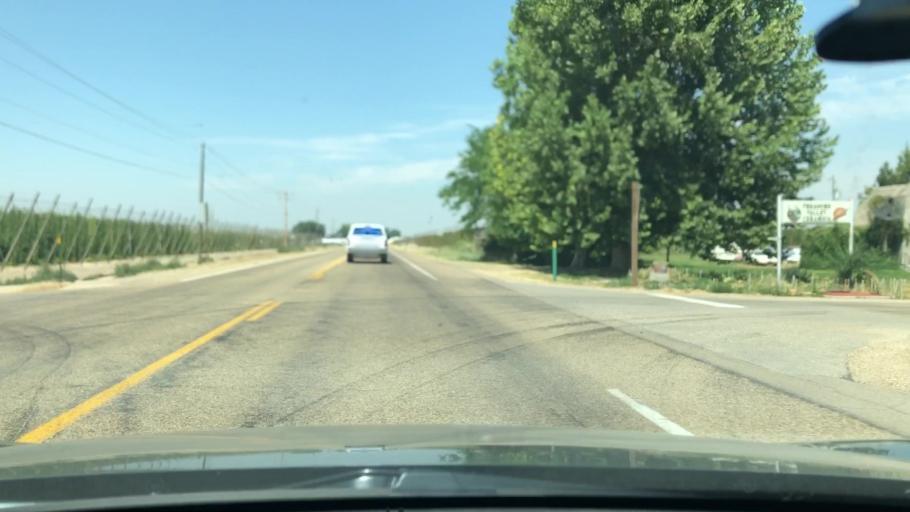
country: US
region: Idaho
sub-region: Canyon County
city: Wilder
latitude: 43.6832
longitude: -116.9120
